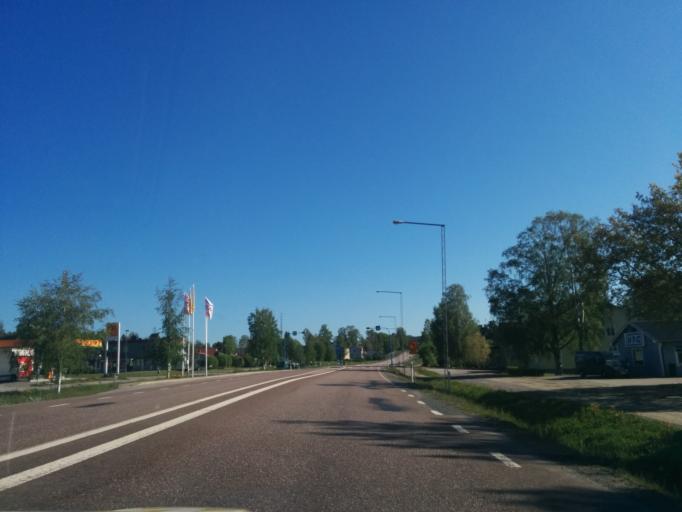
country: SE
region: Vaesternorrland
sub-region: Haernoesands Kommun
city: Haernoesand
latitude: 62.6749
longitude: 17.8415
